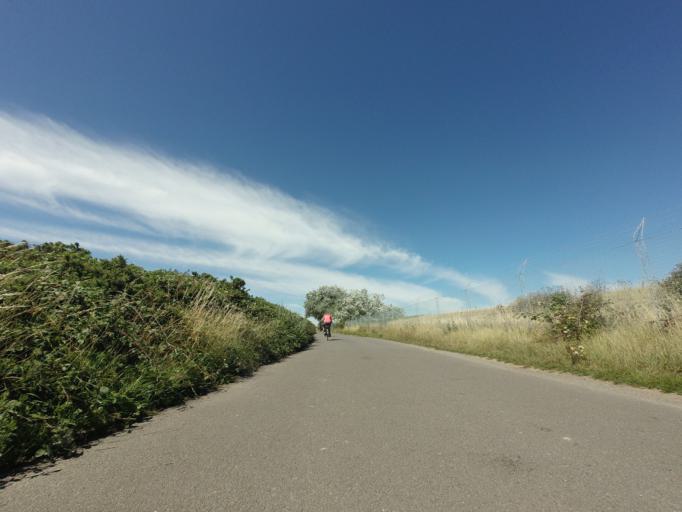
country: GB
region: England
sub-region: Kent
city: Deal
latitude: 51.2517
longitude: 1.3914
